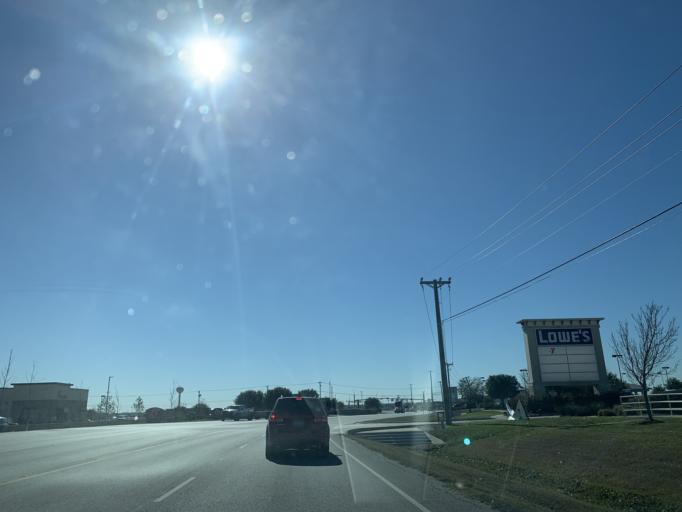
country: US
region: Texas
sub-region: Williamson County
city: Hutto
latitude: 30.5432
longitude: -97.5617
